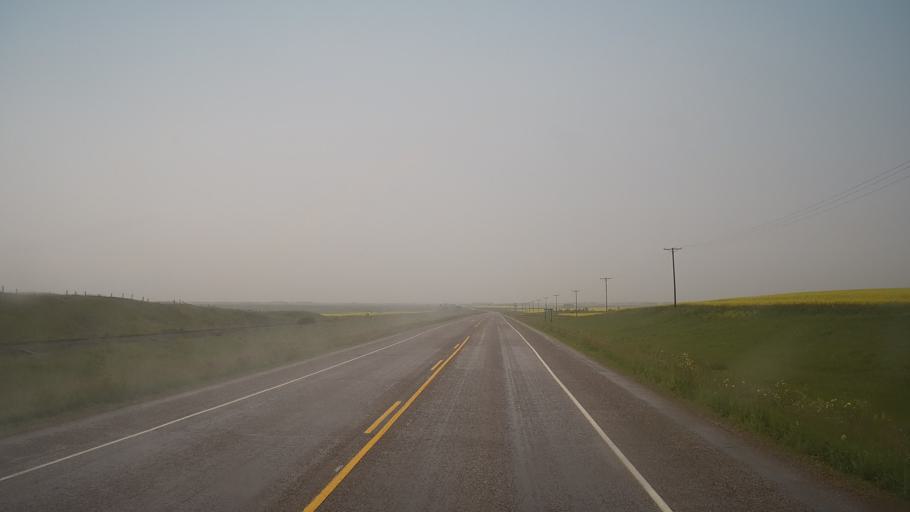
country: CA
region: Saskatchewan
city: Biggar
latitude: 52.1409
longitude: -108.1884
